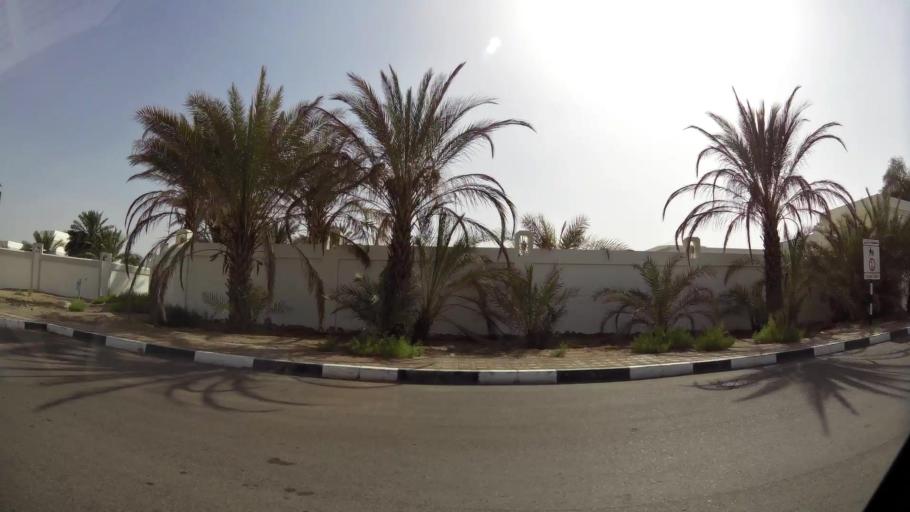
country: AE
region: Abu Dhabi
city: Al Ain
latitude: 24.2433
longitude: 55.6856
